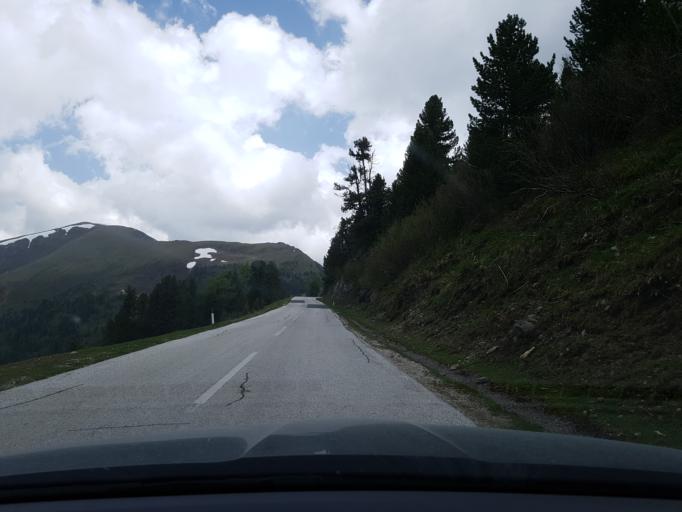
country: AT
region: Carinthia
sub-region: Politischer Bezirk Spittal an der Drau
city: Kleinkirchheim
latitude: 46.8932
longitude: 13.7898
